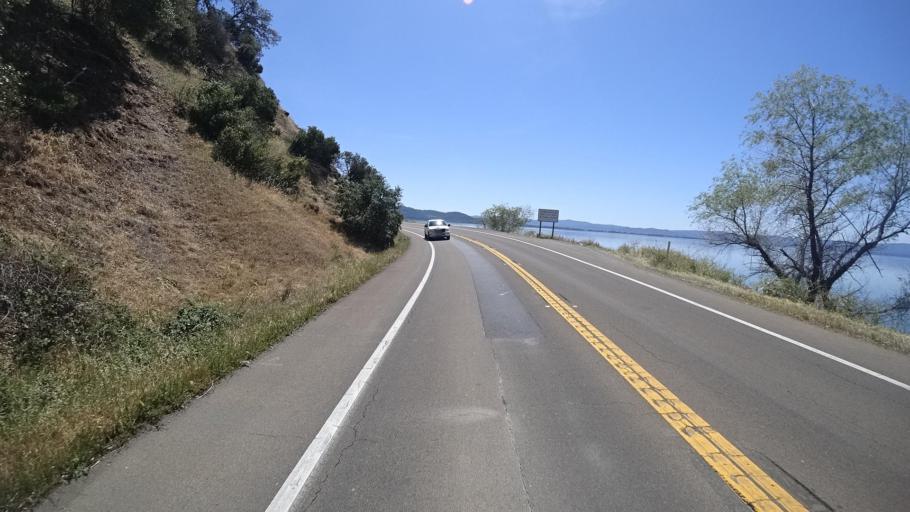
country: US
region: California
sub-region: Lake County
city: Lucerne
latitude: 39.0554
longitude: -122.7825
